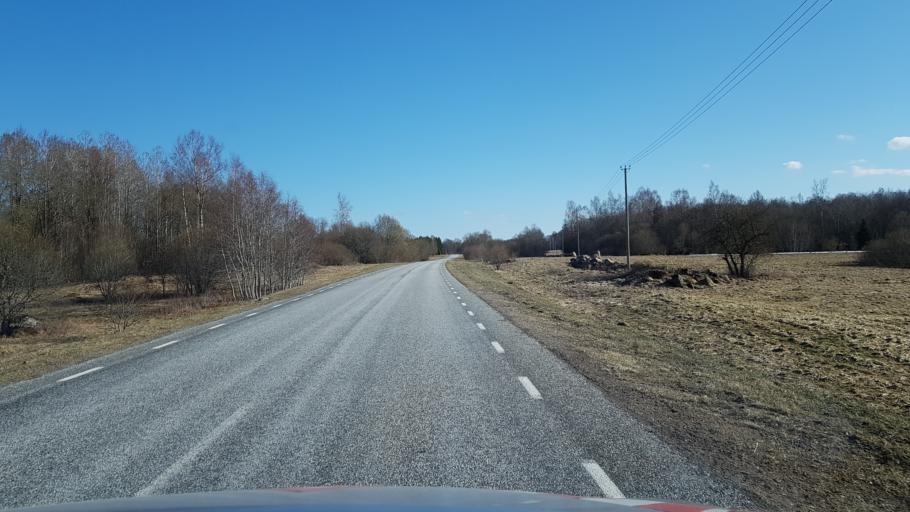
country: EE
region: Laeaene-Virumaa
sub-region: Haljala vald
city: Haljala
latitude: 59.4848
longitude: 26.1519
